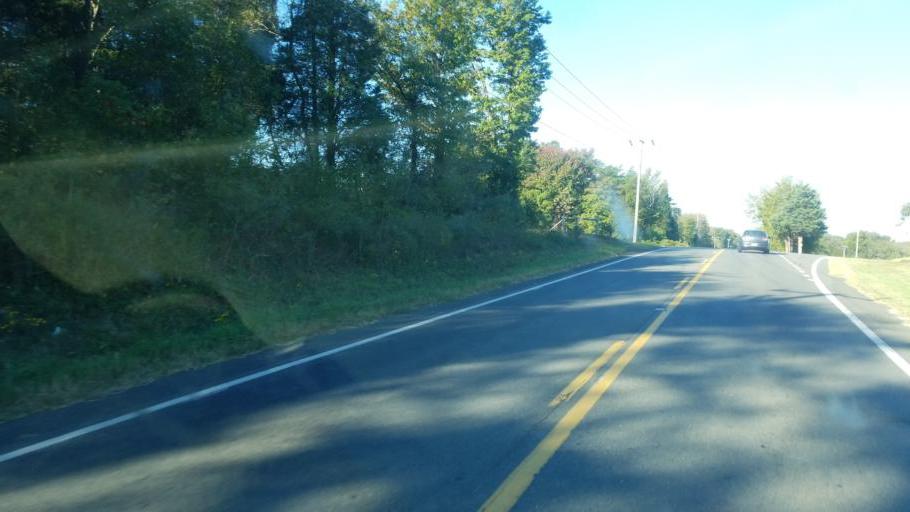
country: US
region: Virginia
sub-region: Fauquier County
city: Bealeton
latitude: 38.5984
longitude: -77.7370
